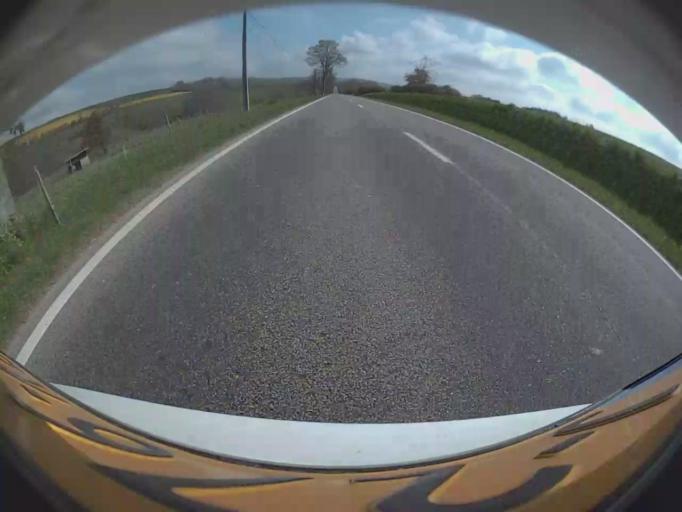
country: BE
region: Wallonia
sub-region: Province de Namur
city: Somme-Leuze
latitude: 50.3271
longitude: 5.3554
